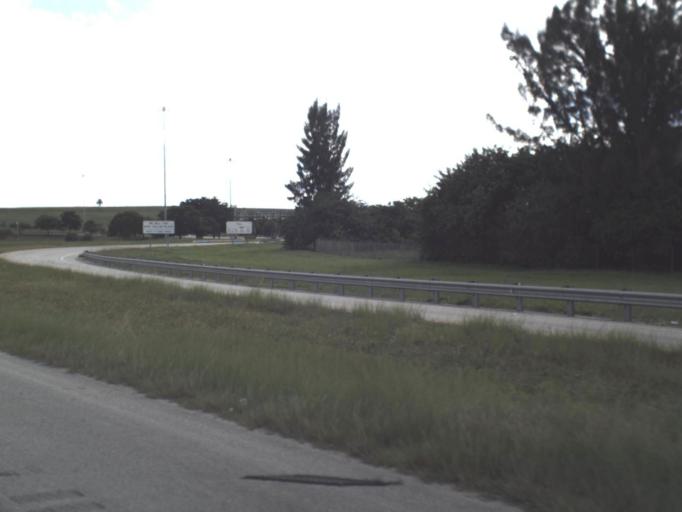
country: US
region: Florida
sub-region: Miami-Dade County
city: Country Club
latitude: 25.9706
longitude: -80.2999
